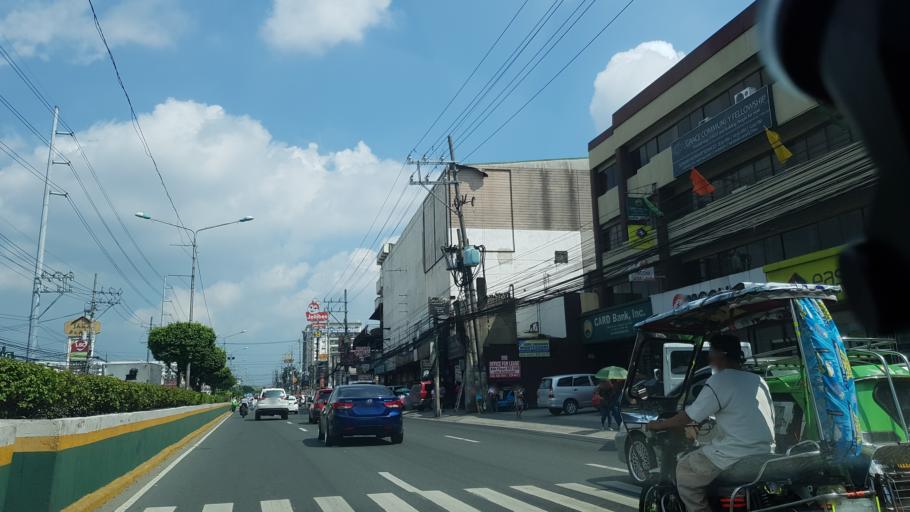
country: PH
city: Sambayanihan People's Village
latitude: 14.4662
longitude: 121.0166
